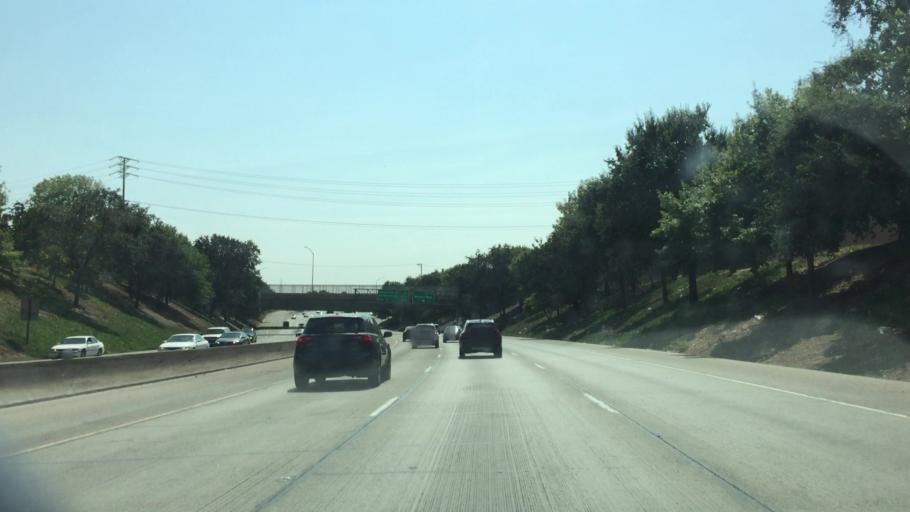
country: US
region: California
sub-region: San Joaquin County
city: August
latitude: 37.9574
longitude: -121.2626
